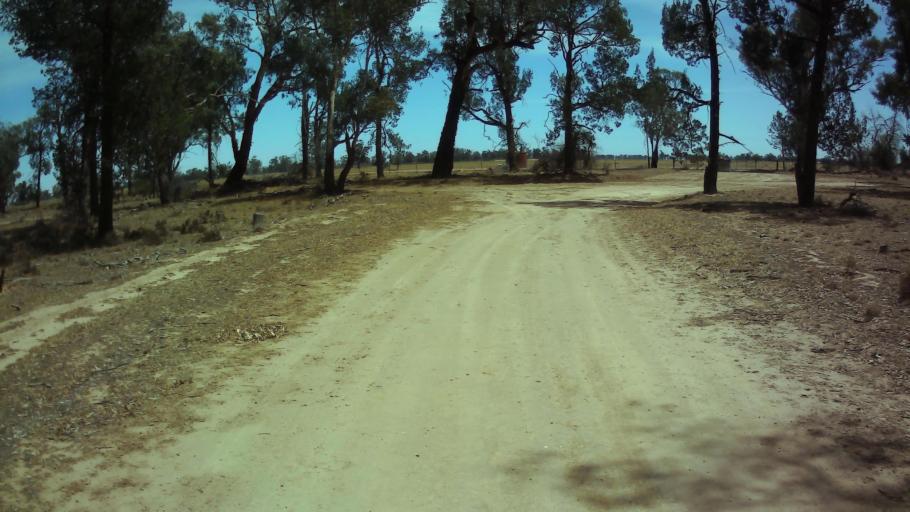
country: AU
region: New South Wales
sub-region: Weddin
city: Grenfell
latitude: -34.0321
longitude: 147.9329
